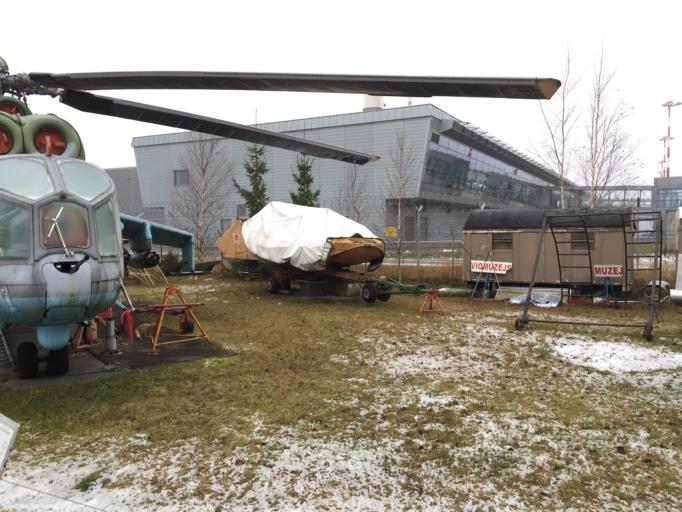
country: LV
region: Babite
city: Pinki
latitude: 56.9251
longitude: 23.9805
